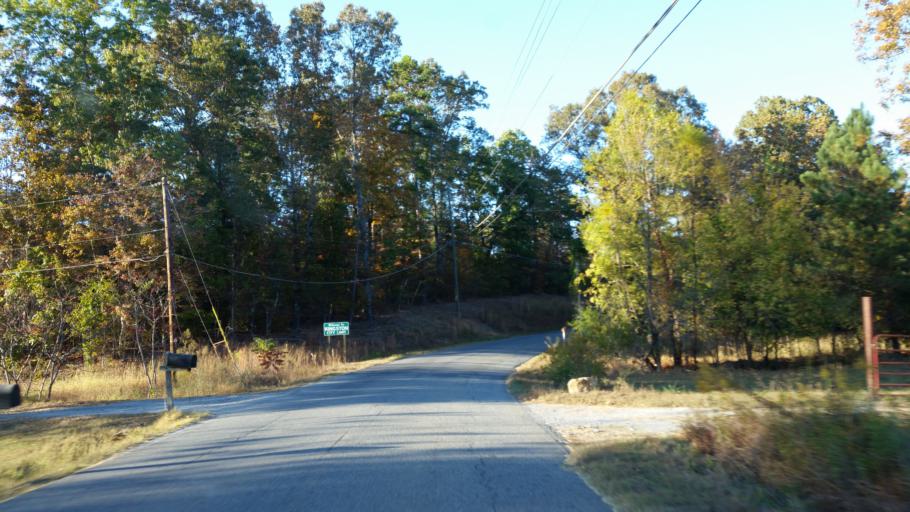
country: US
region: Georgia
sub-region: Bartow County
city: Euharlee
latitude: 34.2203
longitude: -84.9361
